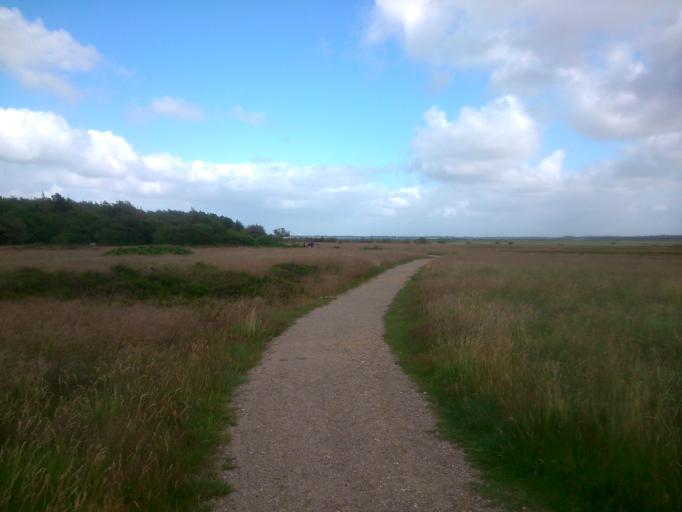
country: DK
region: South Denmark
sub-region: Varde Kommune
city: Oksbol
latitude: 55.6960
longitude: 8.1947
